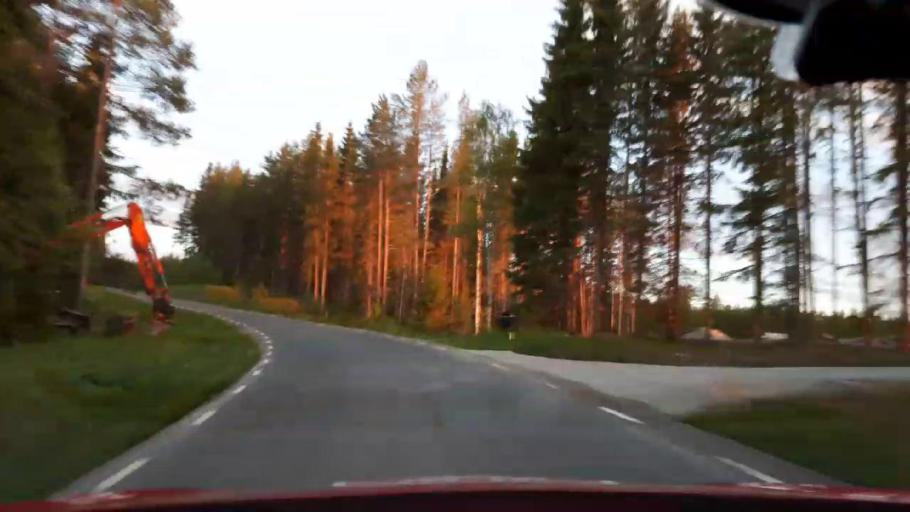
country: SE
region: Jaemtland
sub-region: OEstersunds Kommun
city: Brunflo
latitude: 63.0650
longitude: 14.8033
